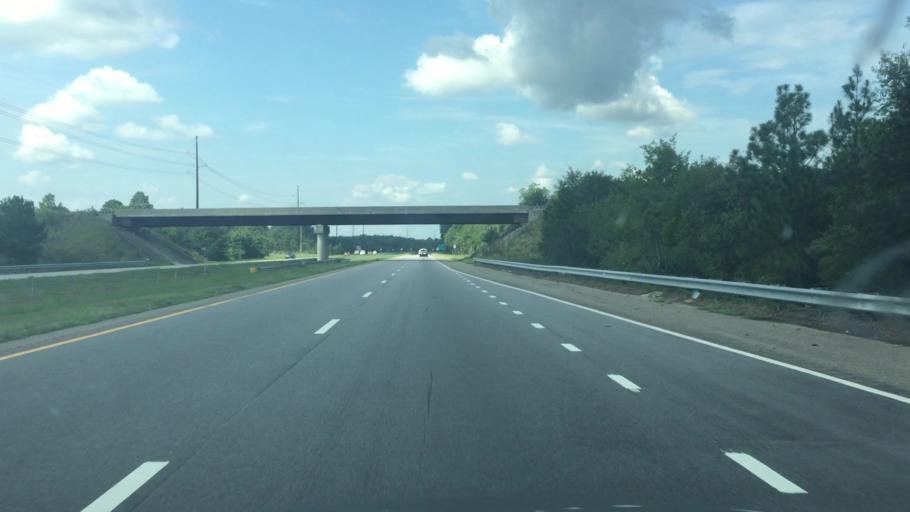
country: US
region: North Carolina
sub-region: Richmond County
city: Hamlet
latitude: 34.8619
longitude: -79.6754
